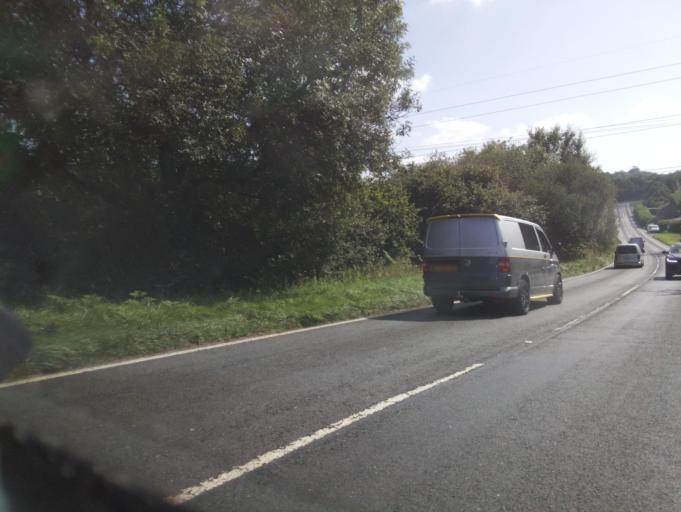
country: GB
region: England
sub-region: Cornwall
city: Pillaton
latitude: 50.4459
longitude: -4.2561
